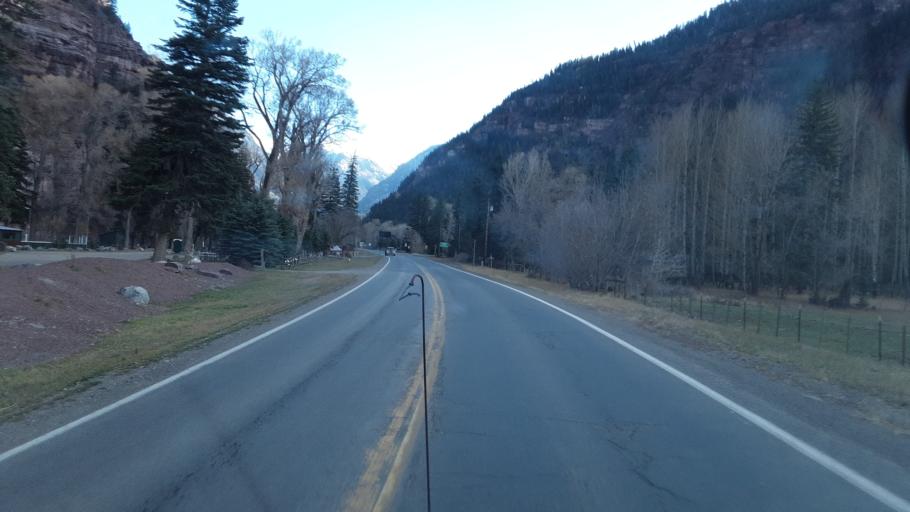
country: US
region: Colorado
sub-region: Ouray County
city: Ouray
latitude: 38.0455
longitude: -107.6821
